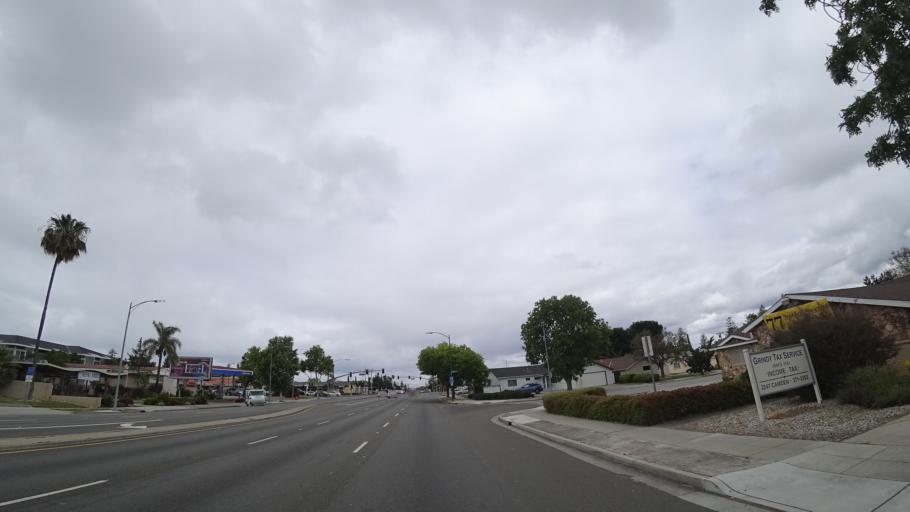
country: US
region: California
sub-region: Santa Clara County
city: Cambrian Park
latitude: 37.2654
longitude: -121.9399
